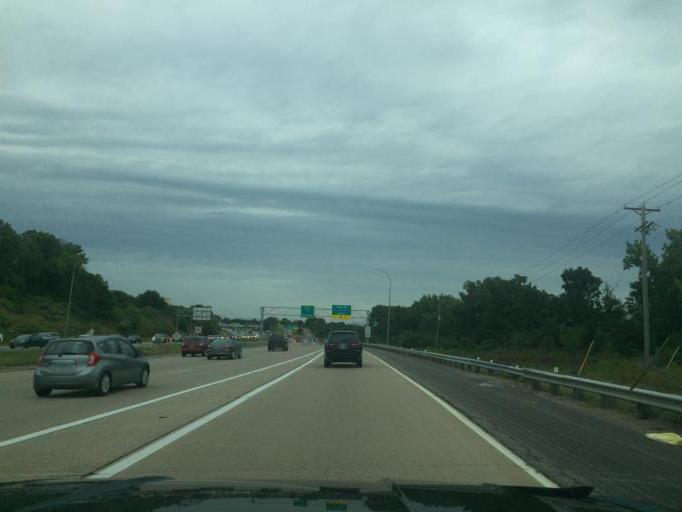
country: US
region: Minnesota
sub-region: Dakota County
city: Mendota Heights
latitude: 44.8654
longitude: -93.2040
